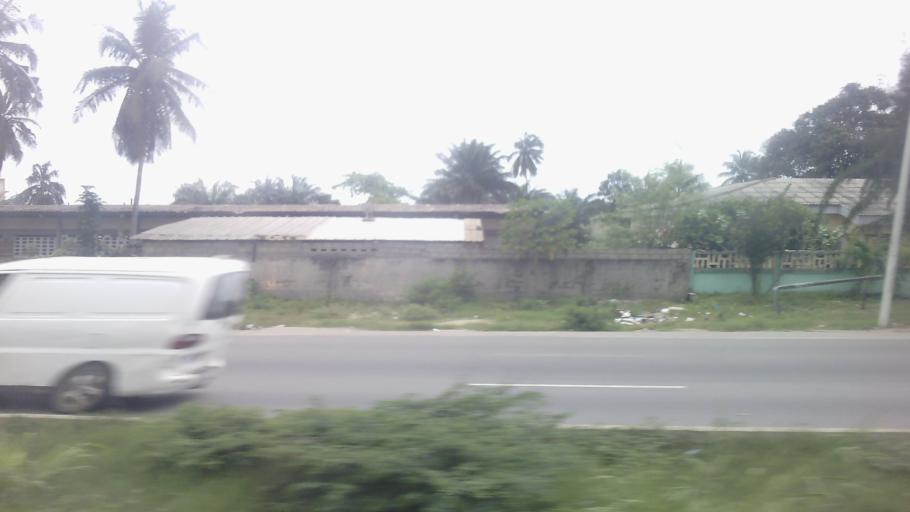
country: CI
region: Lagunes
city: Abidjan
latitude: 5.2527
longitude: -3.9560
